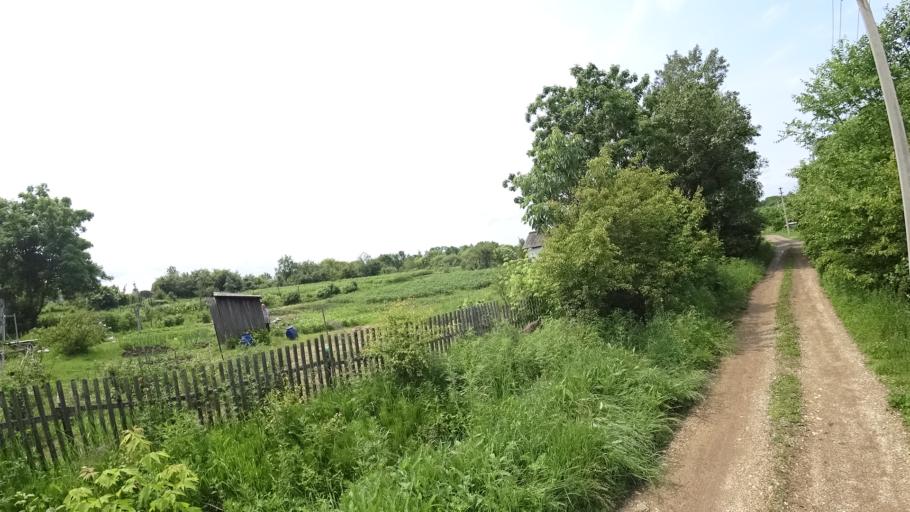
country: RU
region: Primorskiy
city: Novosysoyevka
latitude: 44.2540
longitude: 133.3769
